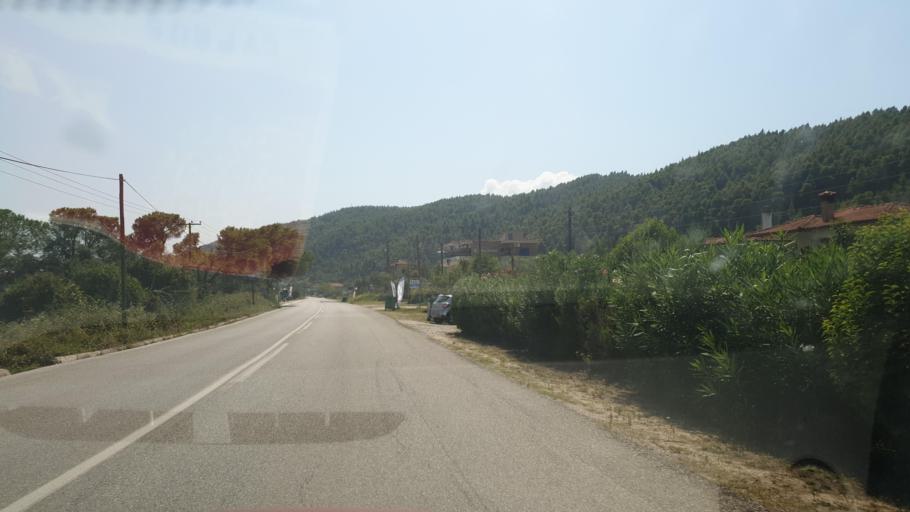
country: GR
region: Central Macedonia
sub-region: Nomos Chalkidikis
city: Neos Marmaras
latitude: 40.1877
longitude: 23.7736
